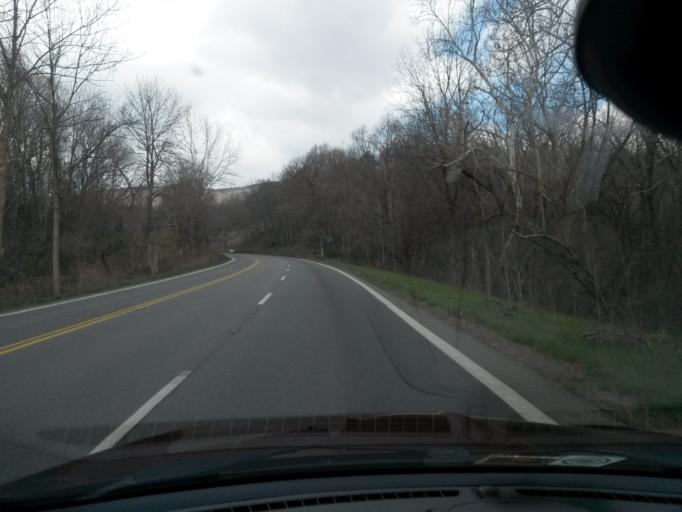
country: US
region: Virginia
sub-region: City of Waynesboro
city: Waynesboro
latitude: 38.0368
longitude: -78.8144
